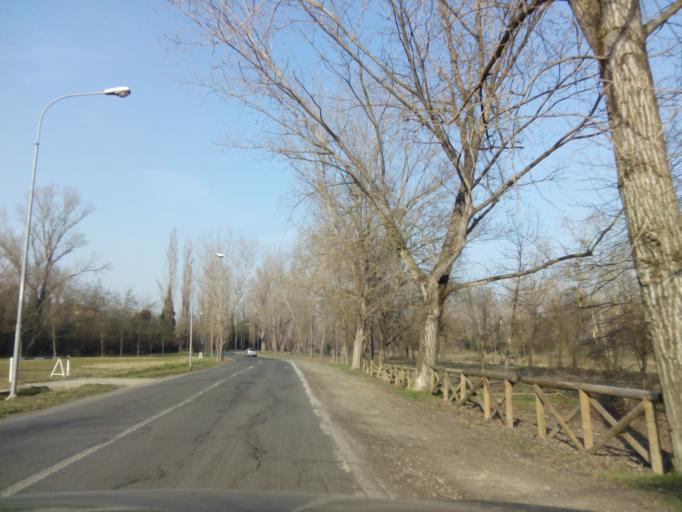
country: IT
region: Emilia-Romagna
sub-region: Provincia di Bologna
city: Imola
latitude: 44.3396
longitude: 11.7024
